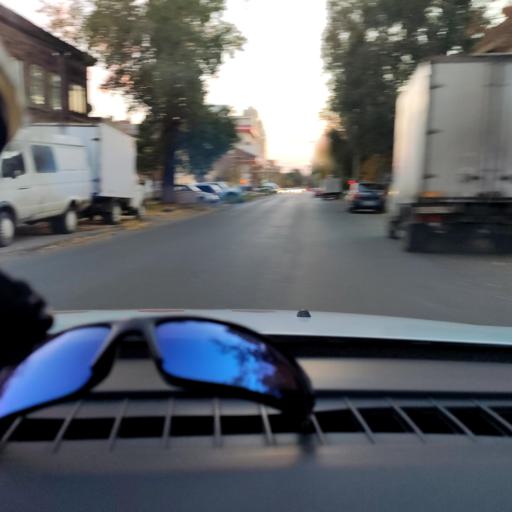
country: RU
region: Samara
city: Samara
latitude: 53.1895
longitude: 50.1108
